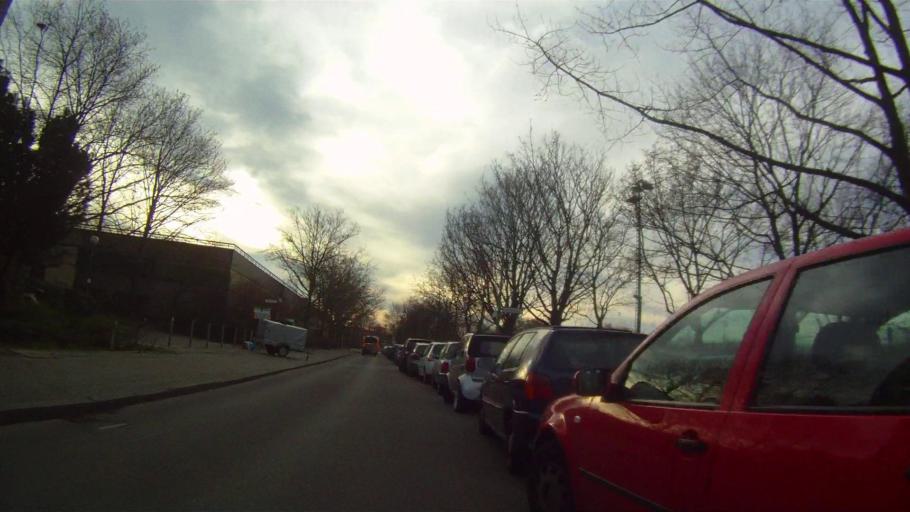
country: DE
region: Berlin
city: Buckow
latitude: 52.4244
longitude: 13.4566
